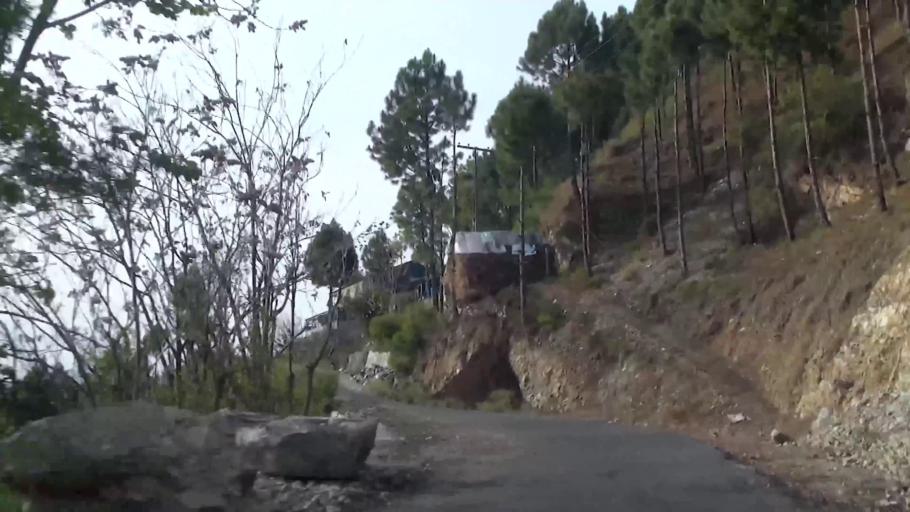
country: PK
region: Azad Kashmir
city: Muzaffarabad
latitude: 34.3626
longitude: 73.5067
